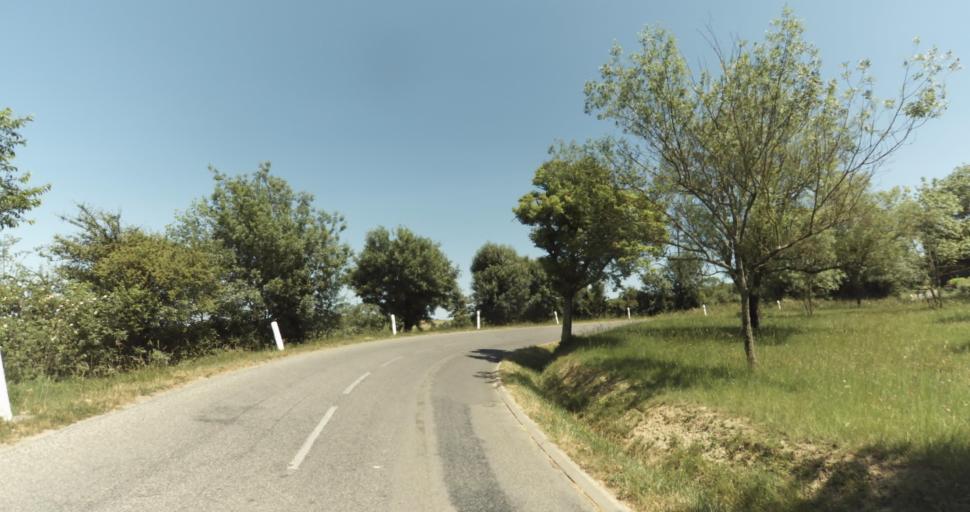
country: FR
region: Midi-Pyrenees
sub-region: Departement de la Haute-Garonne
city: Levignac
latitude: 43.6359
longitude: 1.1774
